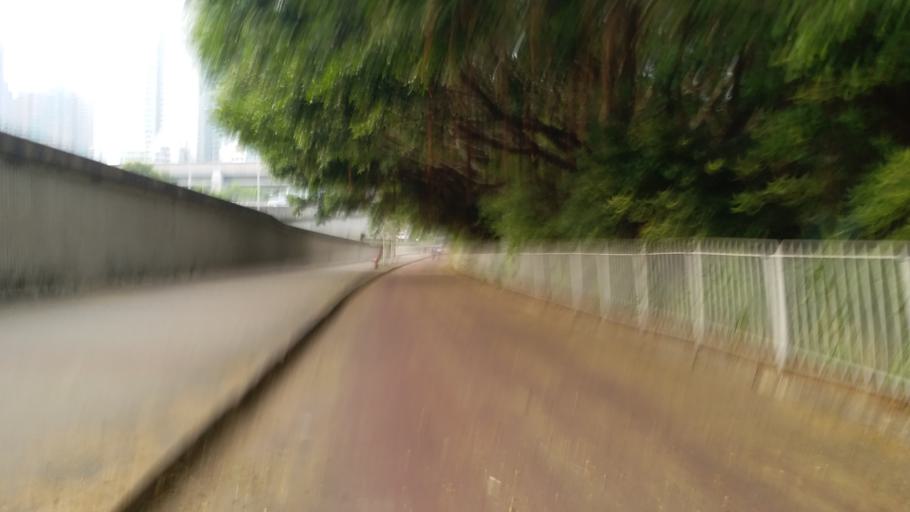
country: HK
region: Yuen Long
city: Yuen Long Kau Hui
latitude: 22.4498
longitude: 114.0101
